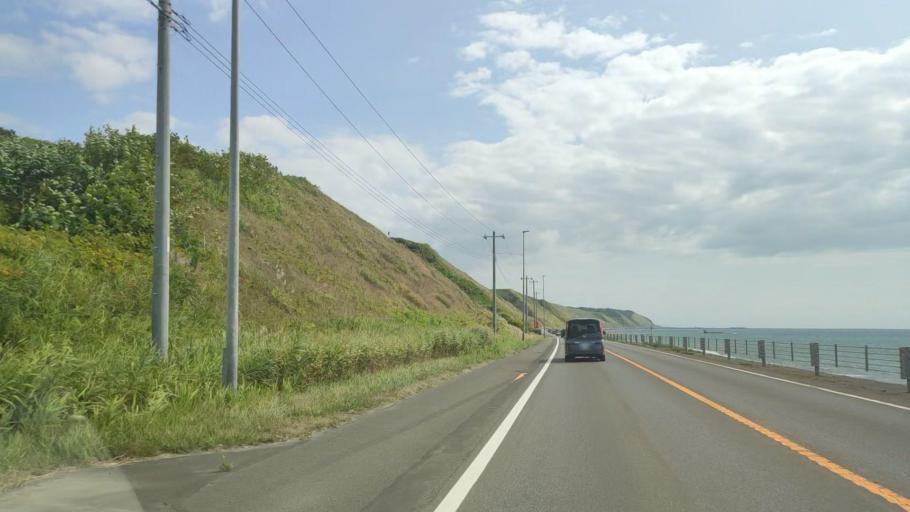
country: JP
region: Hokkaido
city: Rumoi
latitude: 44.2536
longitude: 141.6566
